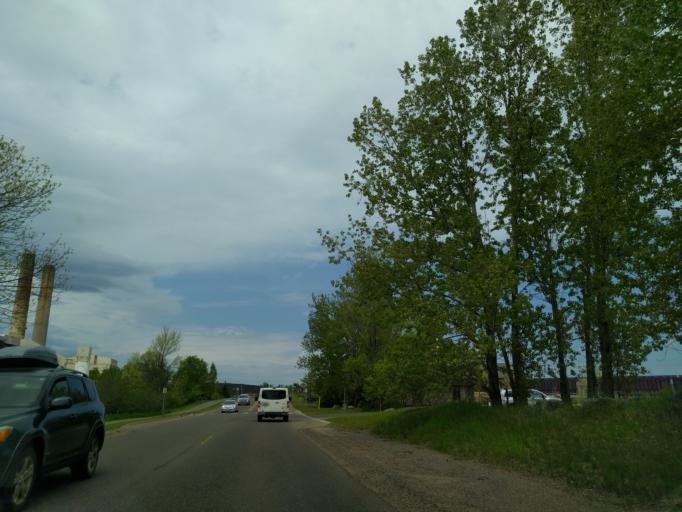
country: US
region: Michigan
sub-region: Marquette County
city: Marquette
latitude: 46.5748
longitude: -87.3933
